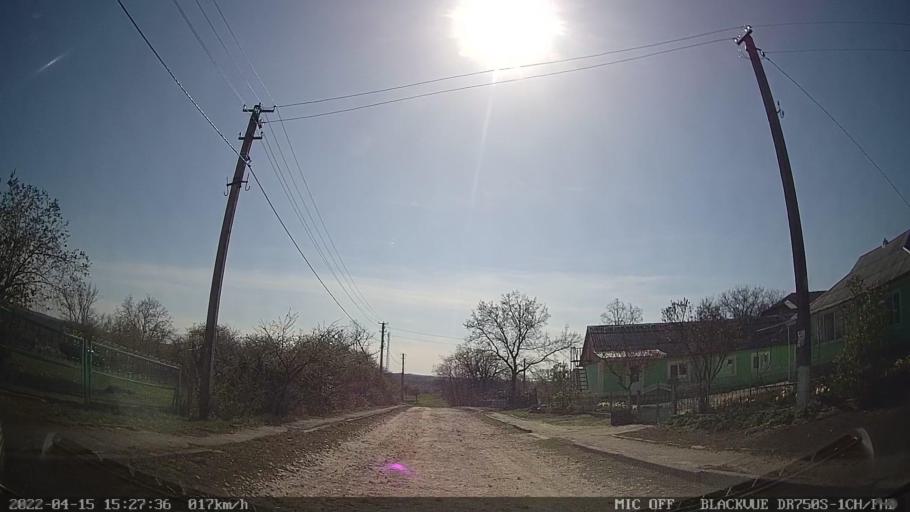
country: MD
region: Raionul Ocnita
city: Otaci
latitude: 48.3597
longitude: 27.9262
